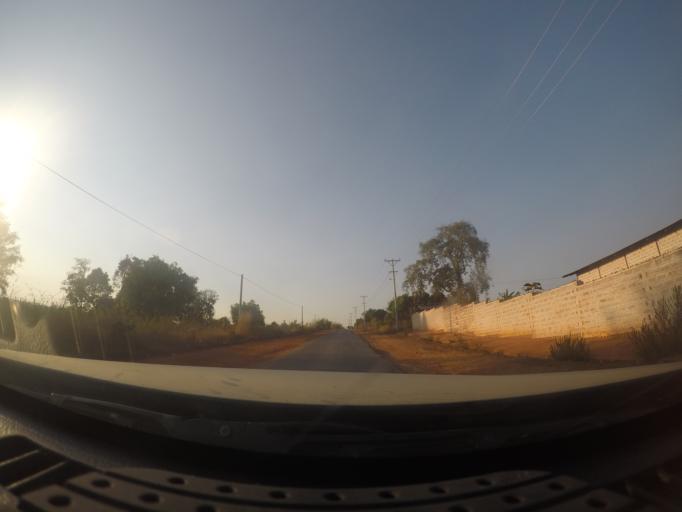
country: MM
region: Shan
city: Taunggyi
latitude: 20.4620
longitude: 97.1290
